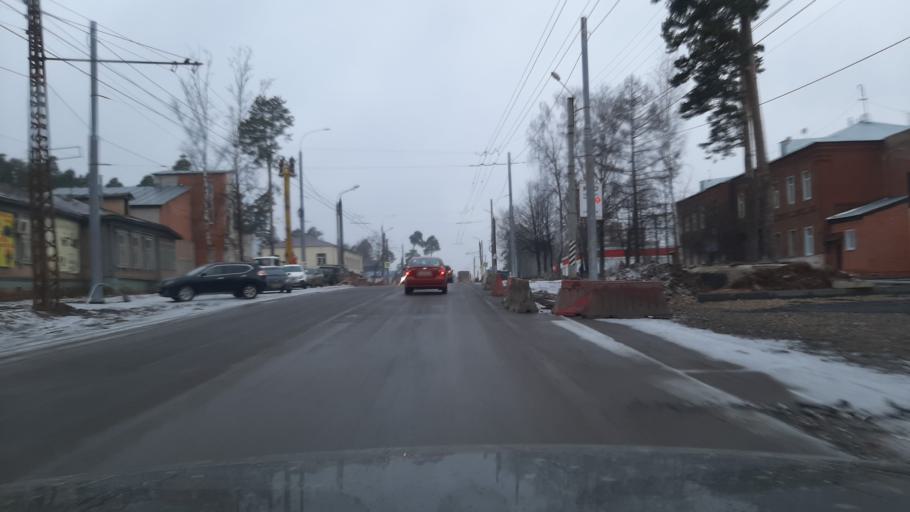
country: RU
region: Ivanovo
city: Kokhma
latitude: 56.9343
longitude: 41.0740
